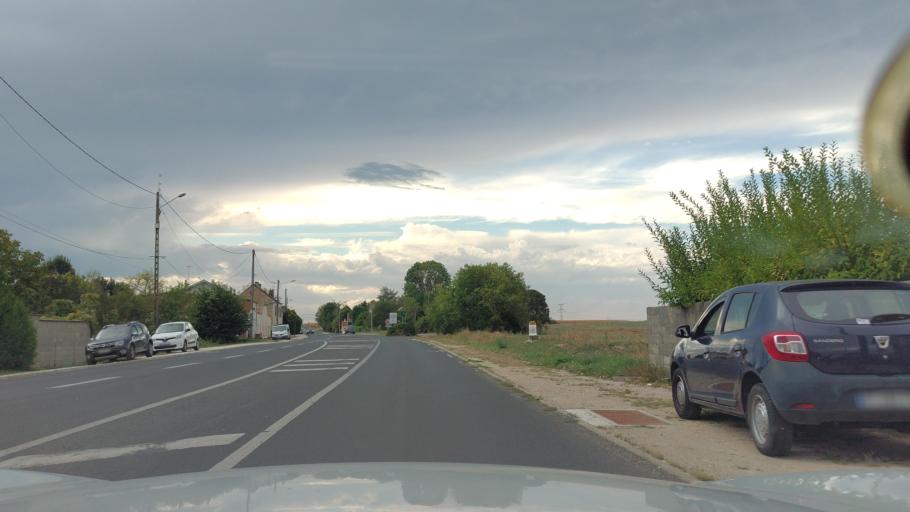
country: FR
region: Ile-de-France
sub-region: Departement de Seine-et-Marne
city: Ozouer-le-Voulgis
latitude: 48.6561
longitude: 2.7558
